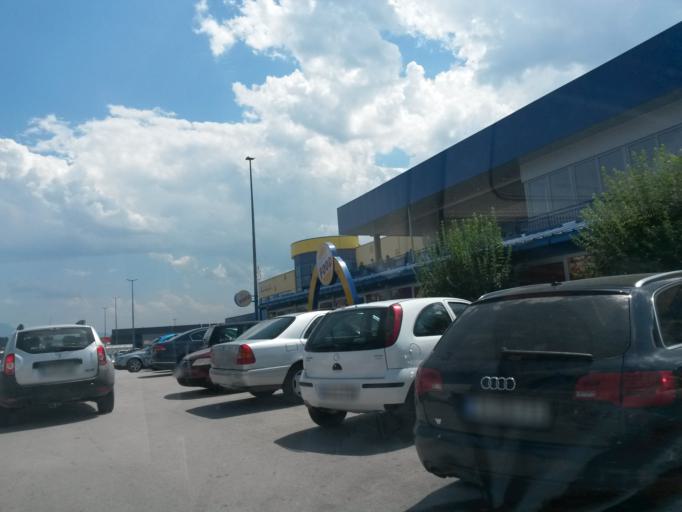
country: BA
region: Federation of Bosnia and Herzegovina
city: Vitez
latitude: 44.1694
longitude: 17.7811
